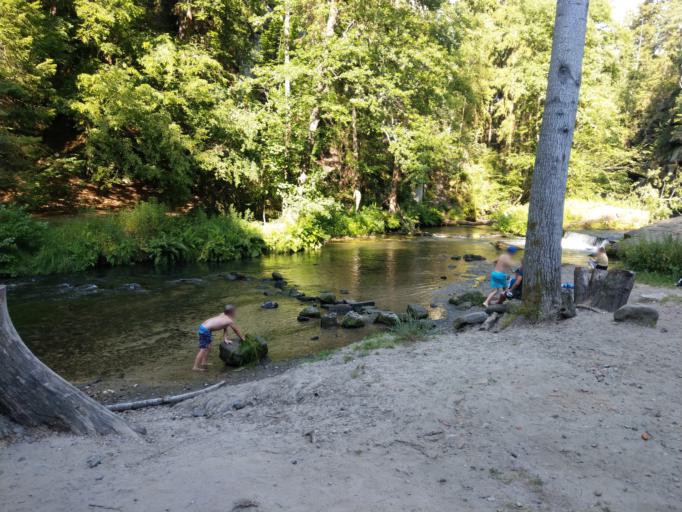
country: CZ
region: Ustecky
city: Ceska Kamenice
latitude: 50.8489
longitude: 14.3475
